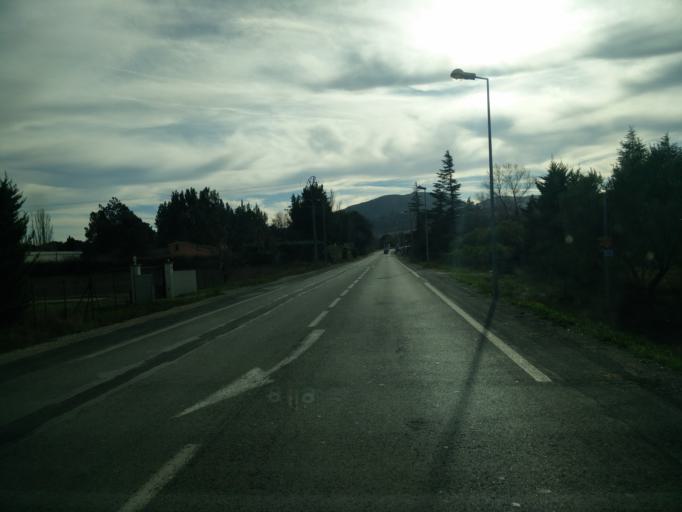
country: FR
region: Provence-Alpes-Cote d'Azur
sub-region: Departement du Var
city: Roquebrune-sur-Argens
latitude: 43.4544
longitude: 6.6334
